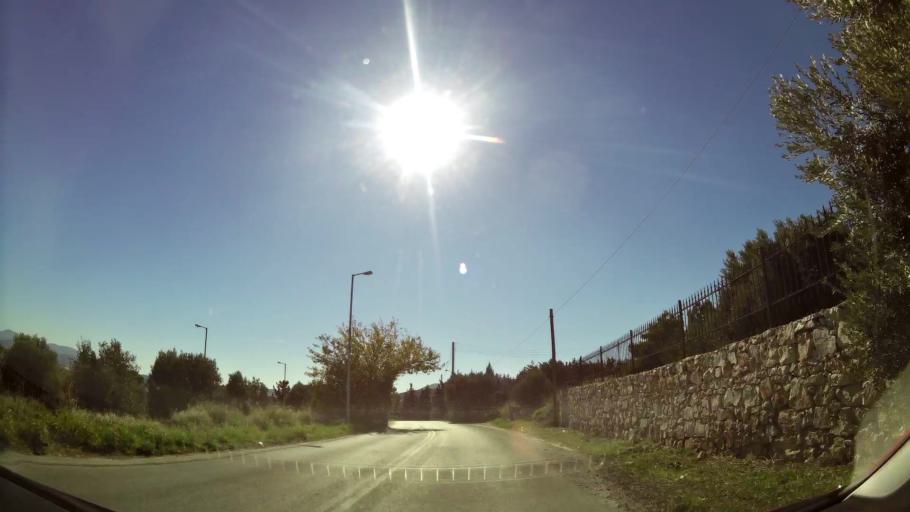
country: GR
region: Attica
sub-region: Nomarchia Anatolikis Attikis
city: Paiania
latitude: 37.9599
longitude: 23.8638
